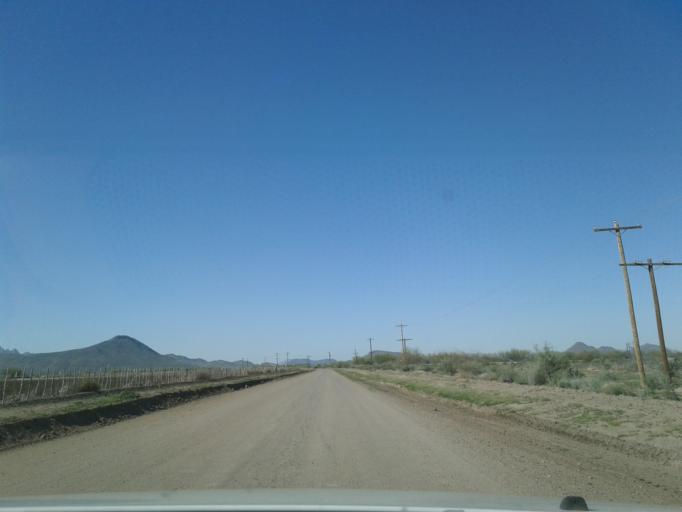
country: US
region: Arizona
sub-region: Pima County
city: Avra Valley
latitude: 32.5527
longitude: -111.3851
